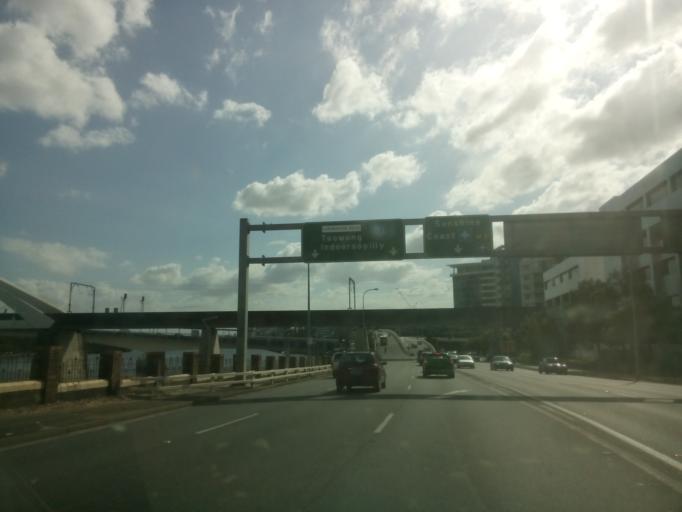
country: AU
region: Queensland
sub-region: Brisbane
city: Milton
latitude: -27.4677
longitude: 153.0137
